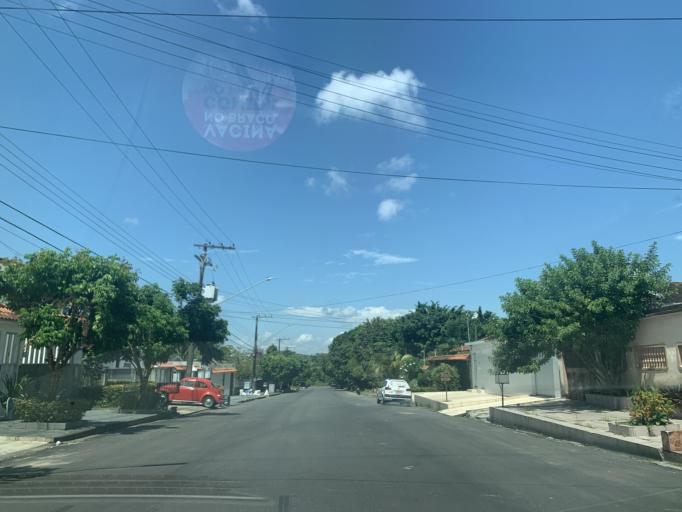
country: BR
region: Amazonas
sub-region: Manaus
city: Manaus
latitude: -3.1104
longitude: -59.9716
